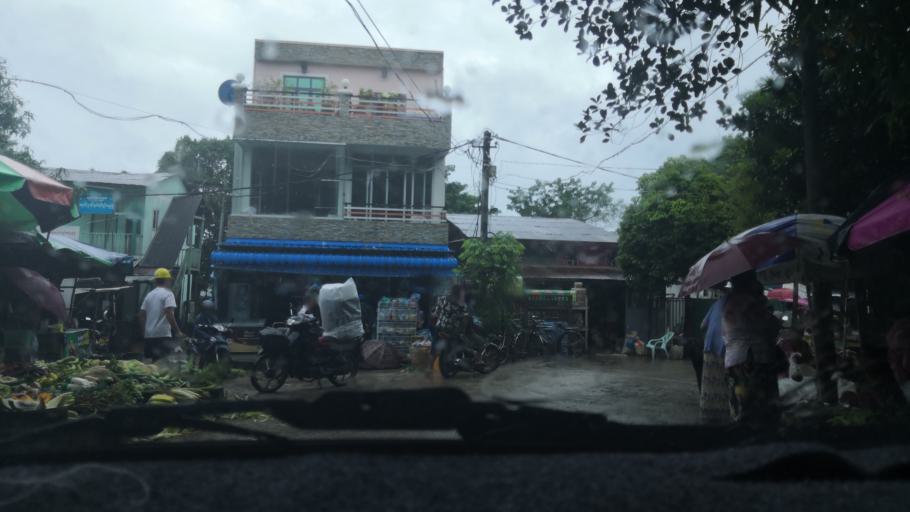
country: MM
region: Yangon
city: Yangon
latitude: 16.8774
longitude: 96.1497
